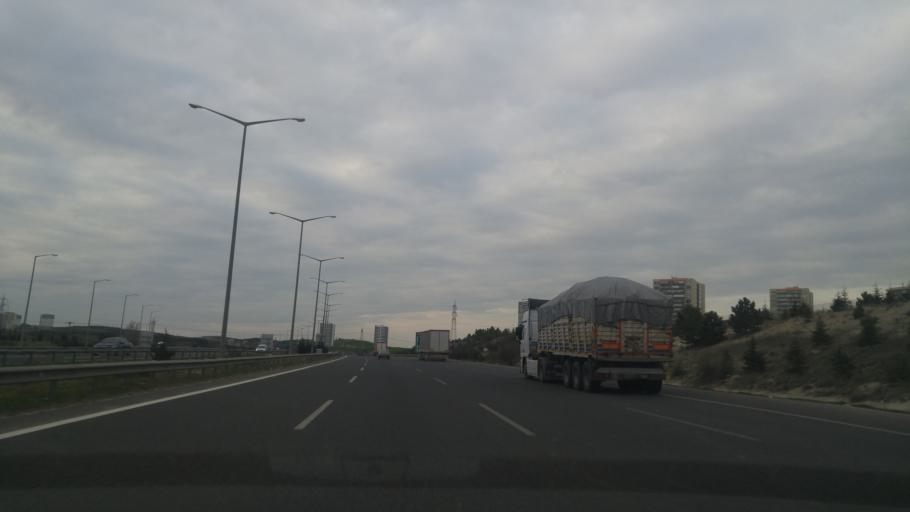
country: TR
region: Ankara
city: Etimesgut
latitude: 39.9985
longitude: 32.6368
